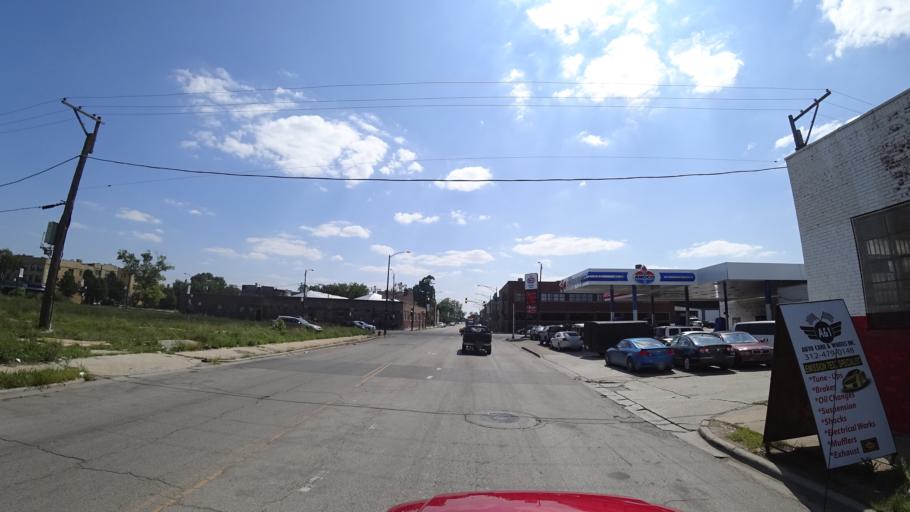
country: US
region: Illinois
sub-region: Cook County
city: Cicero
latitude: 41.8666
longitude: -87.7350
